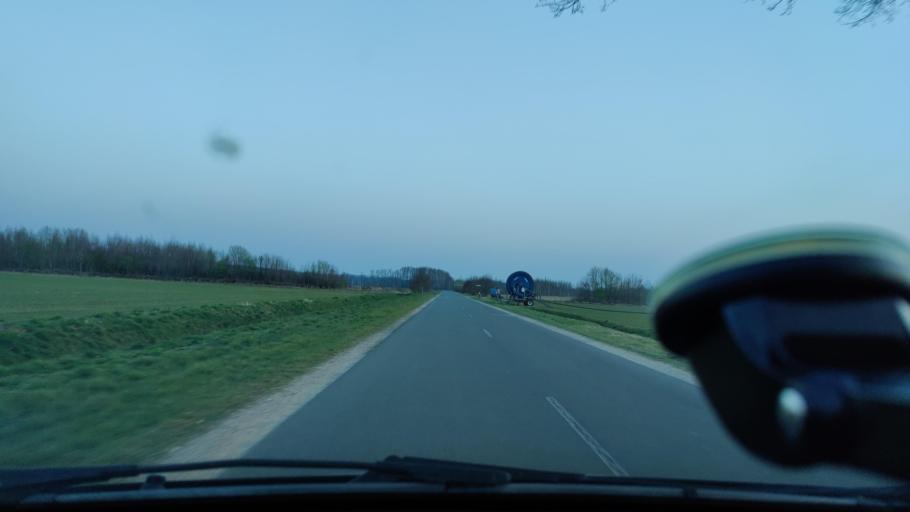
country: NL
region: Limburg
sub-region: Gemeente Bergen
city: Wellerlooi
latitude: 51.5362
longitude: 6.1746
